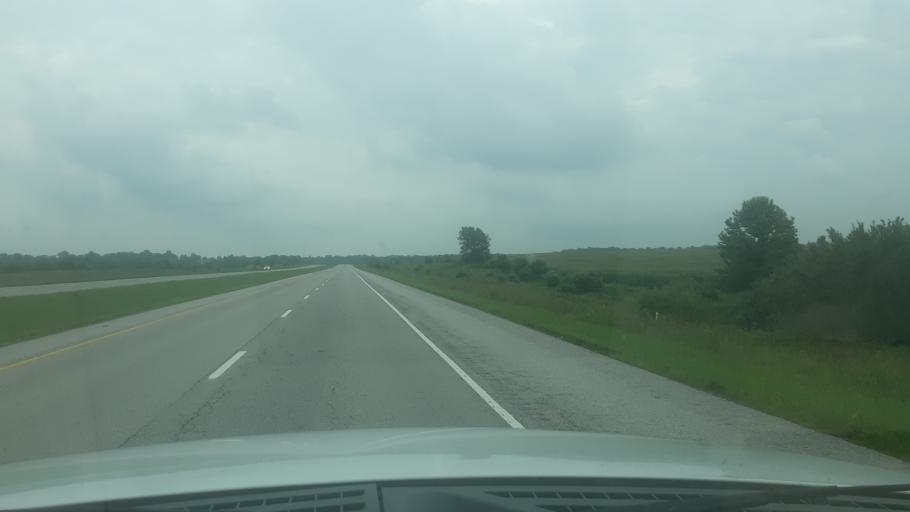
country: US
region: Illinois
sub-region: Saline County
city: Harrisburg
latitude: 37.7298
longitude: -88.5928
